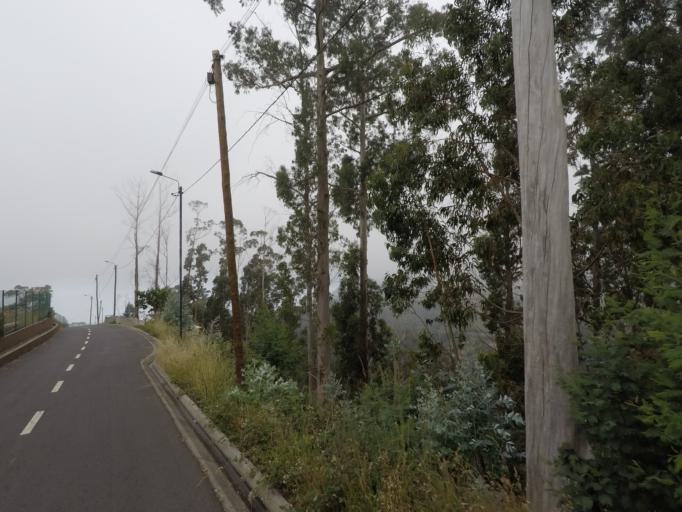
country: PT
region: Madeira
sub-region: Camara de Lobos
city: Curral das Freiras
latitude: 32.6882
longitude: -16.9477
